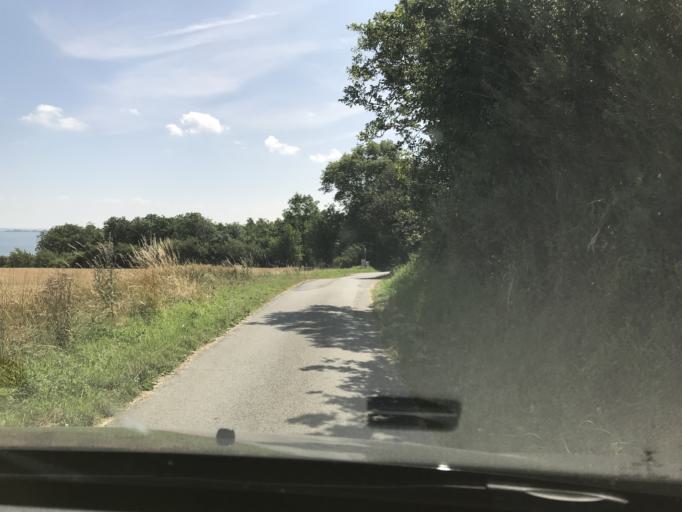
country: DK
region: South Denmark
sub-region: AEro Kommune
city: AEroskobing
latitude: 54.9032
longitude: 10.3247
